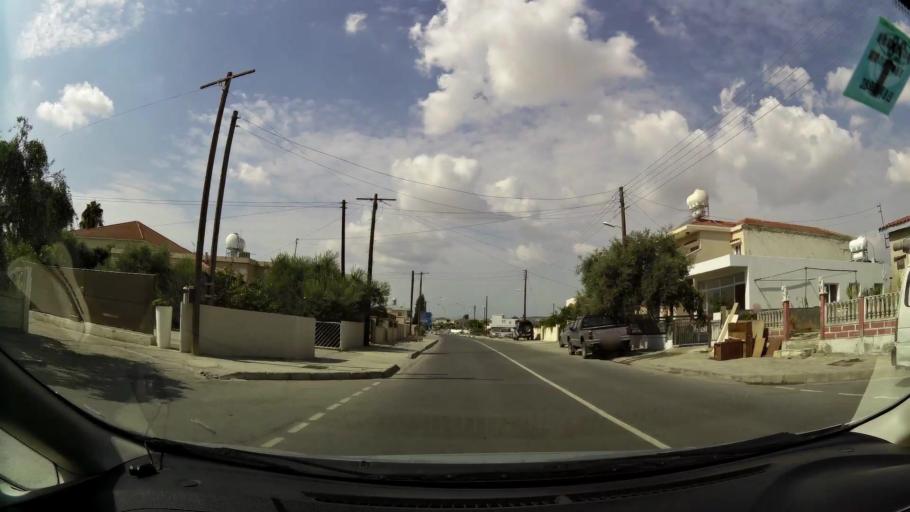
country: CY
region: Larnaka
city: Aradippou
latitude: 34.9498
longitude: 33.5762
